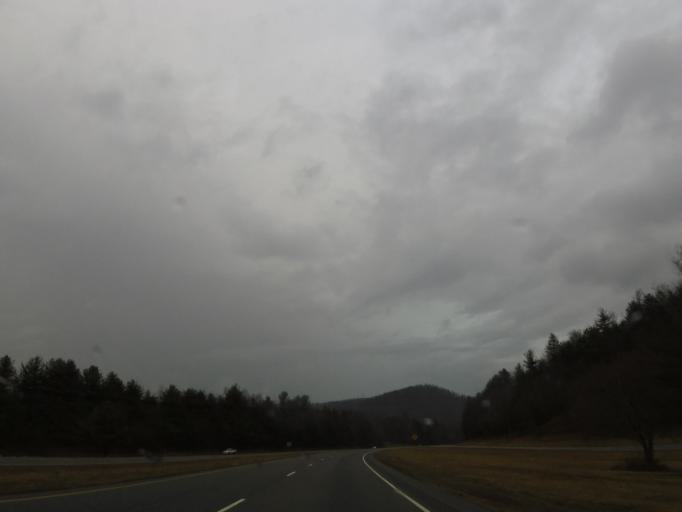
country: US
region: North Carolina
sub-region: Henderson County
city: Flat Rock
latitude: 35.2167
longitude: -82.4444
